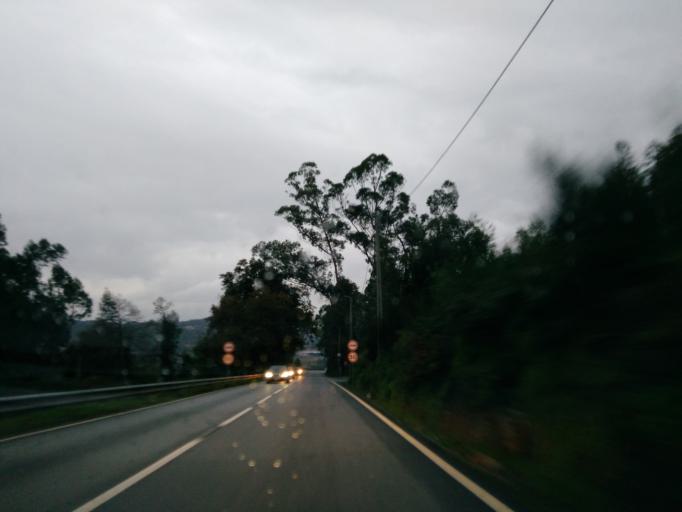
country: PT
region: Braga
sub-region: Braga
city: Oliveira
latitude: 41.4616
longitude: -8.4936
